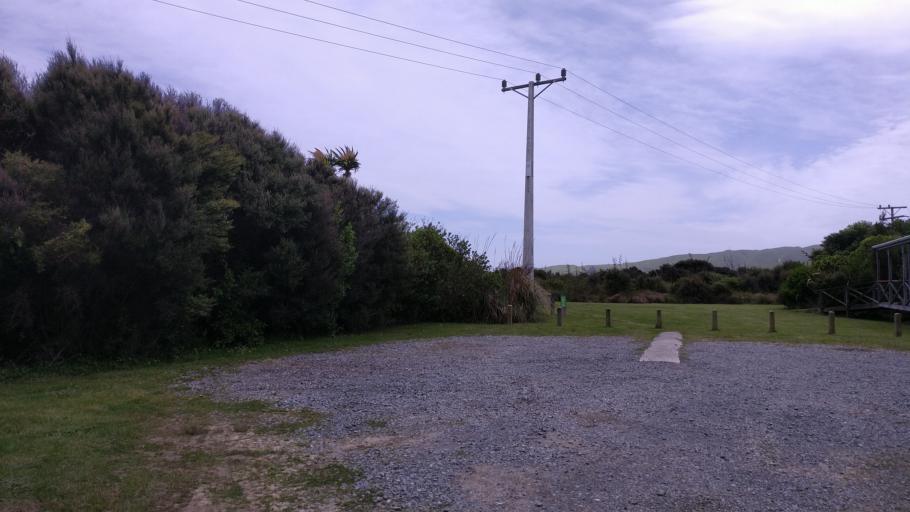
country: NZ
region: Wellington
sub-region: Porirua City
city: Porirua
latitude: -41.1052
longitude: 174.9160
